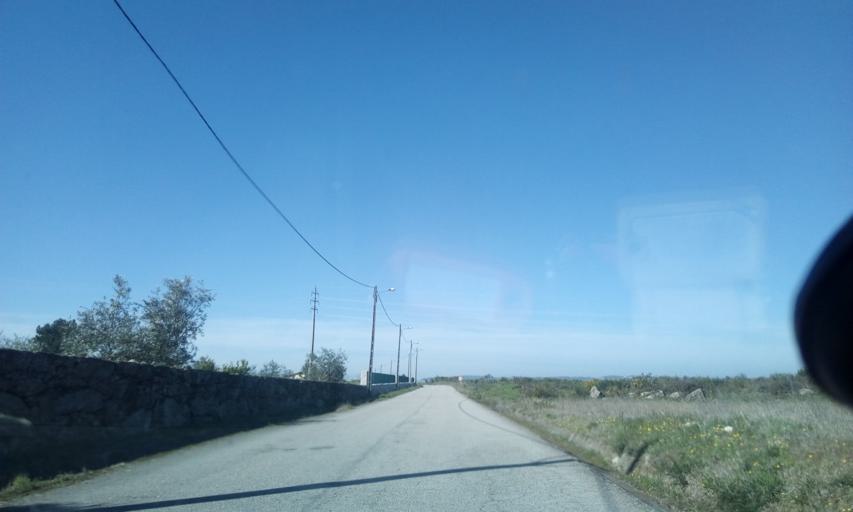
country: PT
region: Guarda
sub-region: Celorico da Beira
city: Celorico da Beira
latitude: 40.5920
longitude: -7.4422
